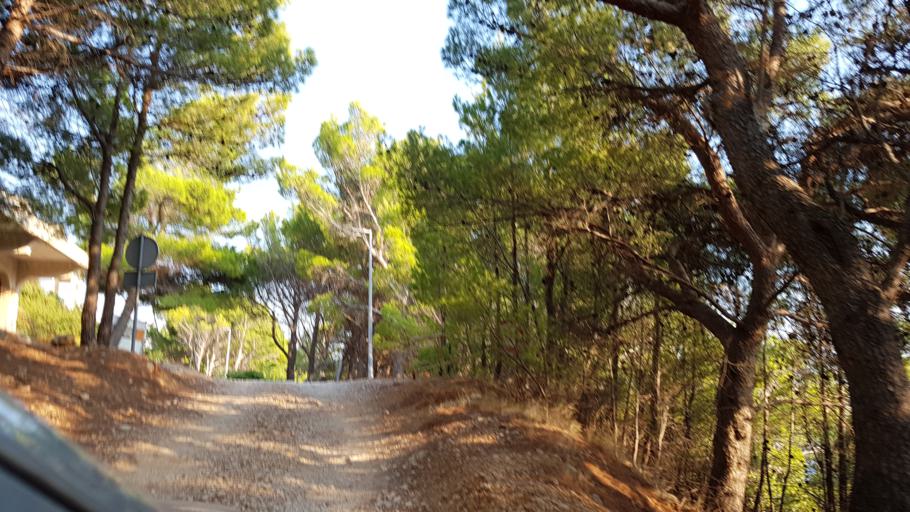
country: HR
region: Splitsko-Dalmatinska
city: Donja Brela
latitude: 43.3884
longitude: 16.8978
